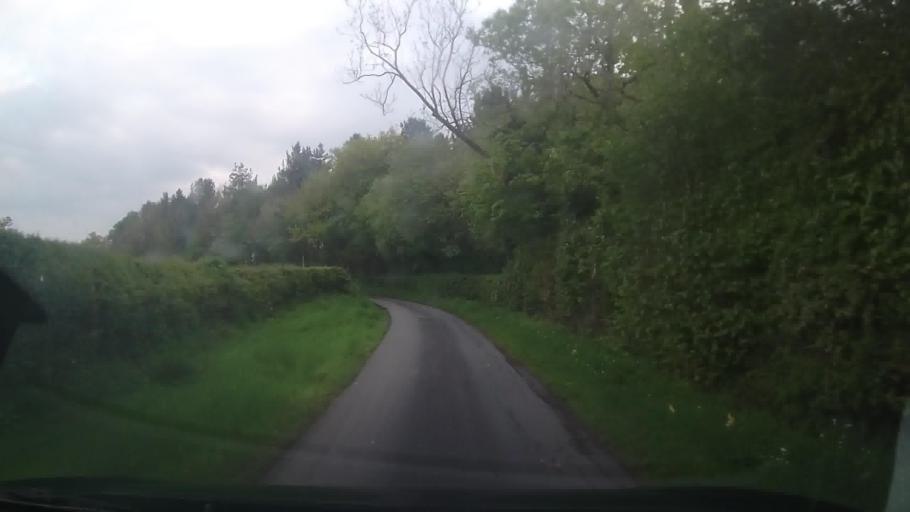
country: GB
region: England
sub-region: Shropshire
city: Ellesmere
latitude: 52.9391
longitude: -2.8651
